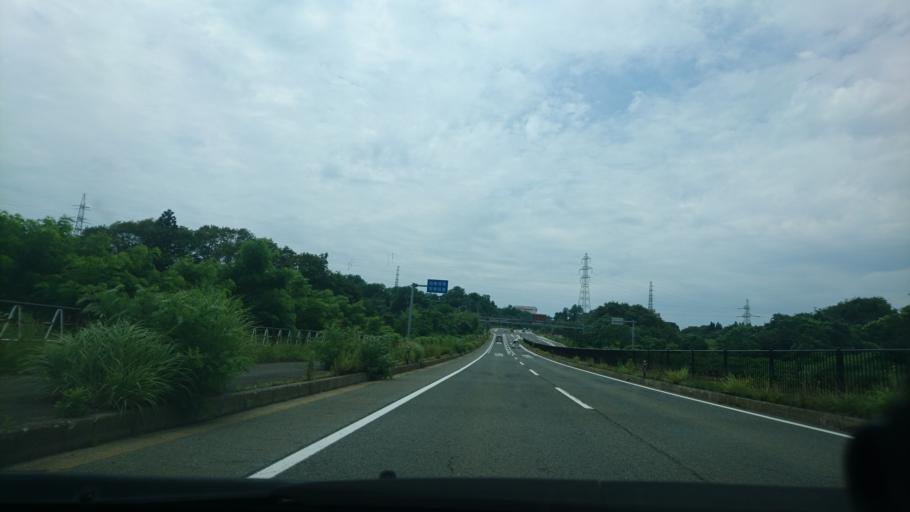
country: JP
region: Akita
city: Akita
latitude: 39.6633
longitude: 140.1822
